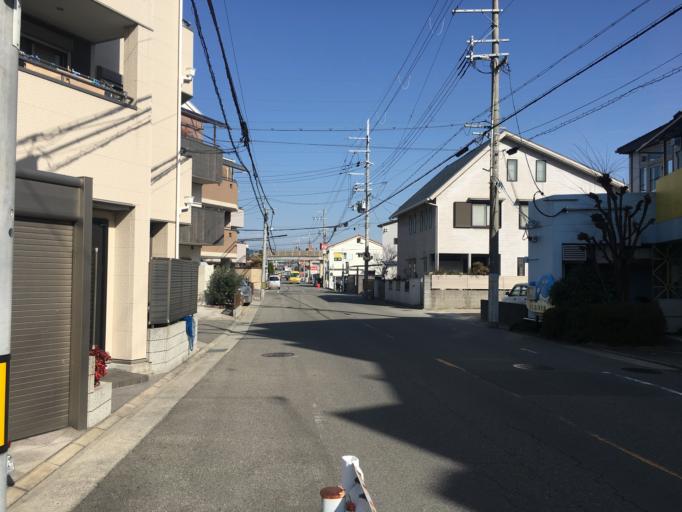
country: JP
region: Hyogo
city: Itami
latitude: 34.7702
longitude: 135.3778
